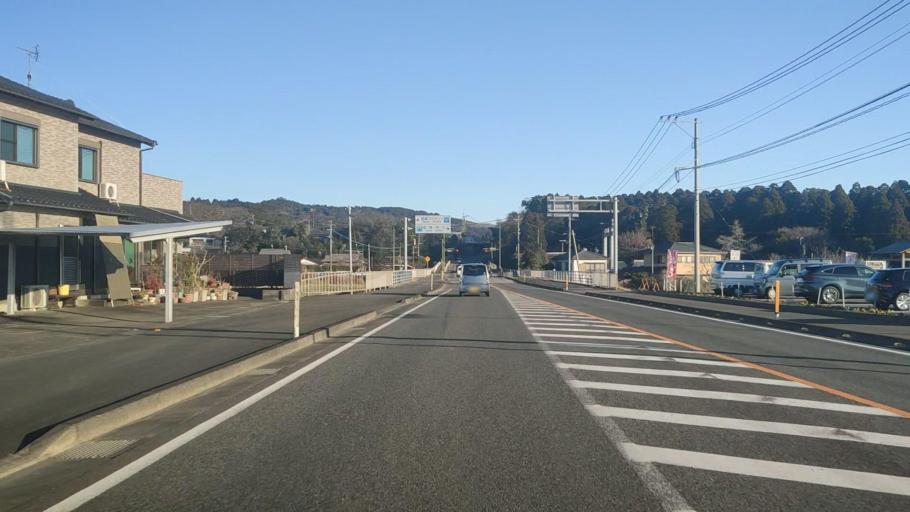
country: JP
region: Miyazaki
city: Takanabe
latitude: 32.2604
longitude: 131.5570
